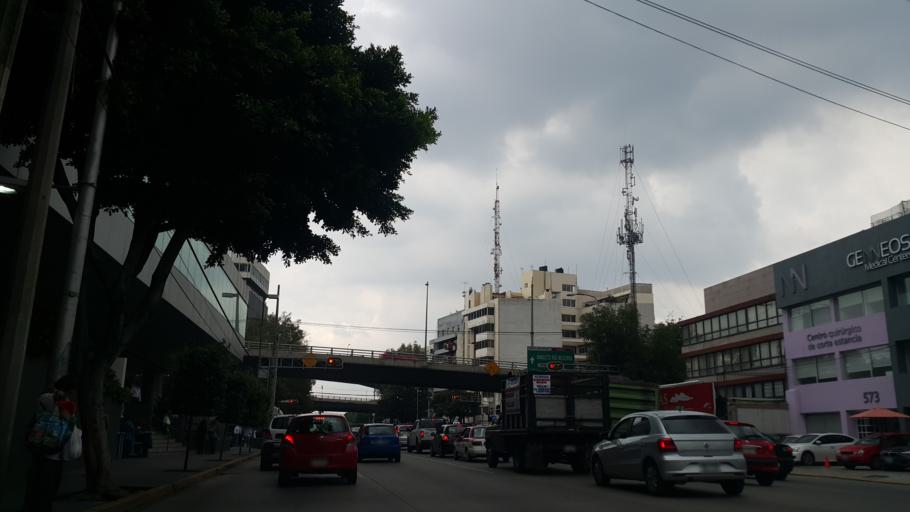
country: MX
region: Mexico City
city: Colonia del Valle
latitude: 19.3833
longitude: -99.1840
